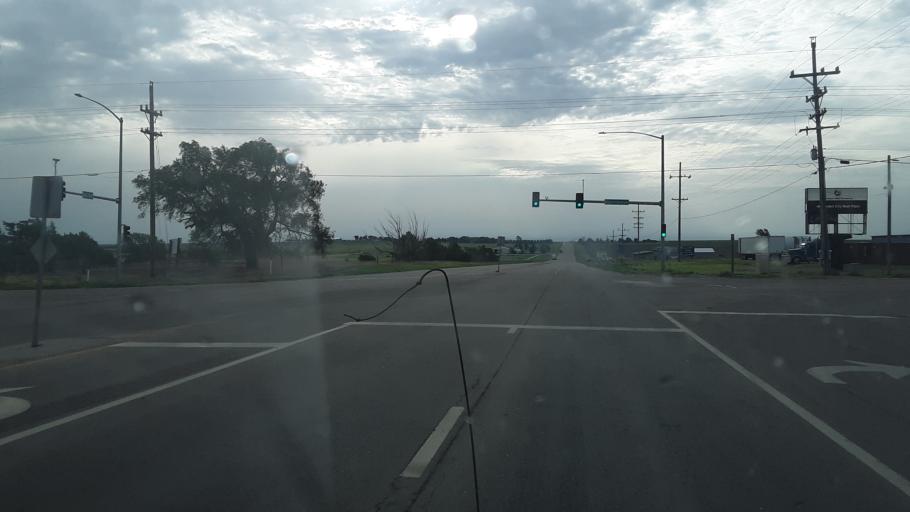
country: US
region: Kansas
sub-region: Finney County
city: Garden City
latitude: 37.9602
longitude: -100.8112
